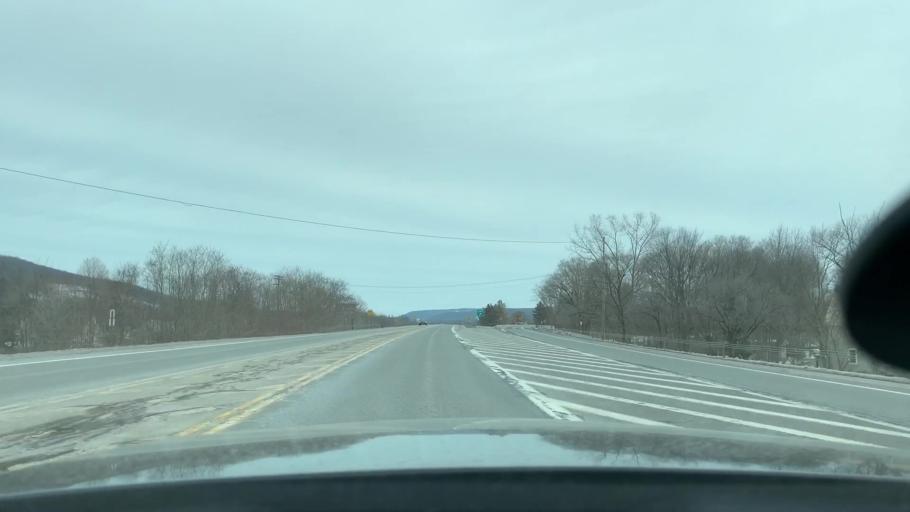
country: US
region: New York
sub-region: Herkimer County
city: Frankfort
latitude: 43.0243
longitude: -75.0577
